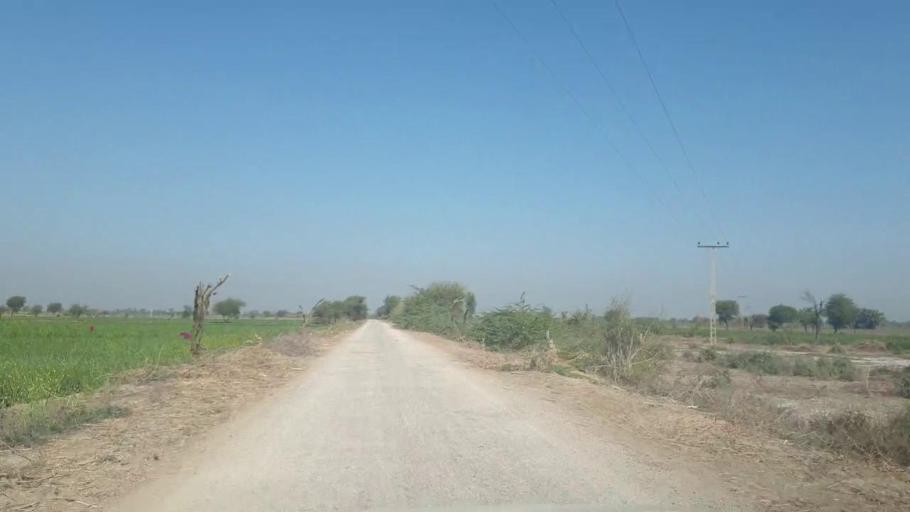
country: PK
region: Sindh
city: Mirpur Khas
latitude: 25.5038
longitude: 69.1726
